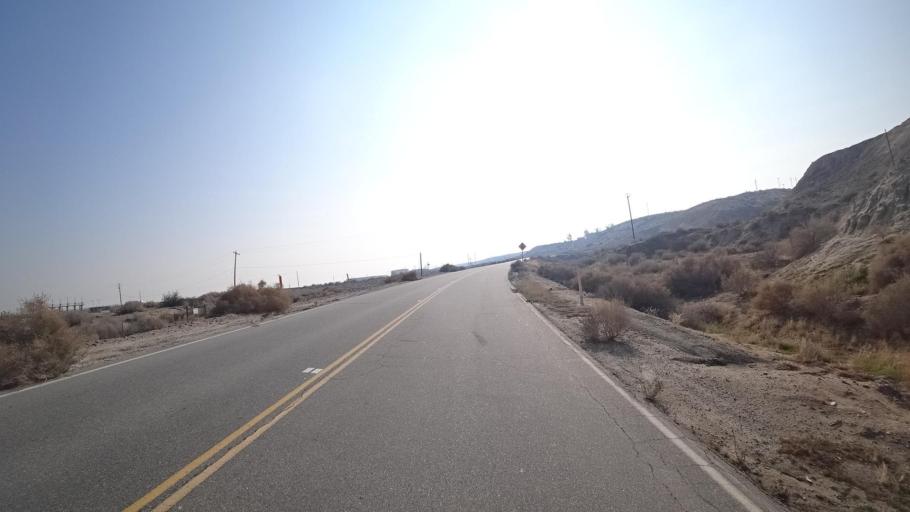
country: US
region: California
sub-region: Kern County
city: Ford City
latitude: 35.2687
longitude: -119.3118
